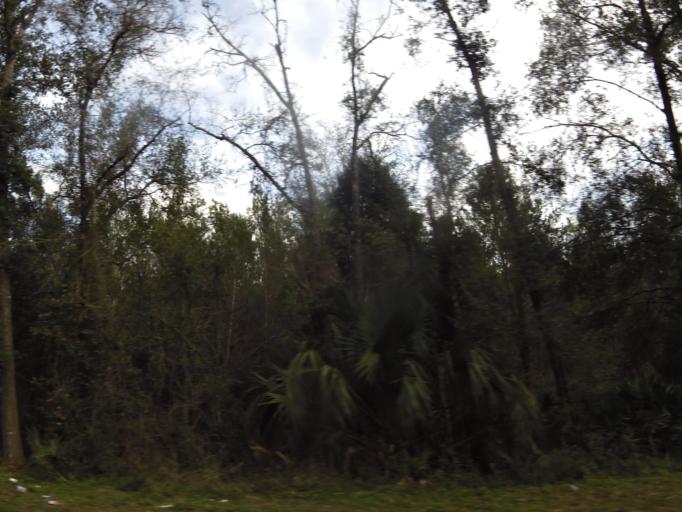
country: US
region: Florida
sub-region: Volusia County
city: Orange City
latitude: 28.9533
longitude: -81.2657
